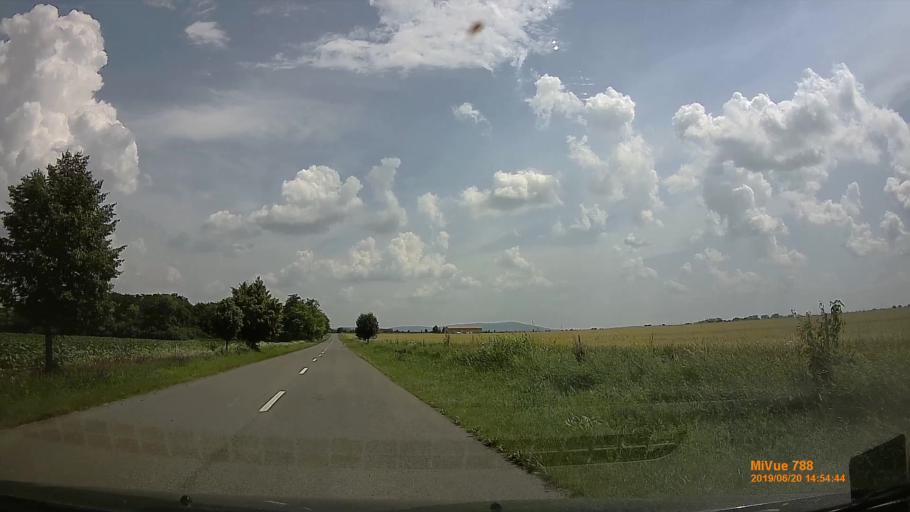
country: HU
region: Baranya
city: Kozarmisleny
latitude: 45.9965
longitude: 18.2437
